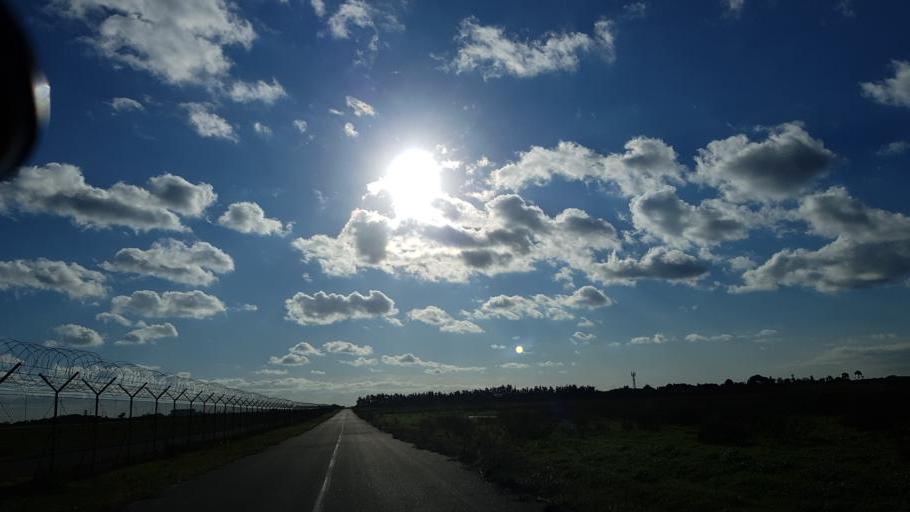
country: IT
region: Apulia
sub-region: Provincia di Brindisi
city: Materdomini
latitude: 40.6713
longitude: 17.9282
